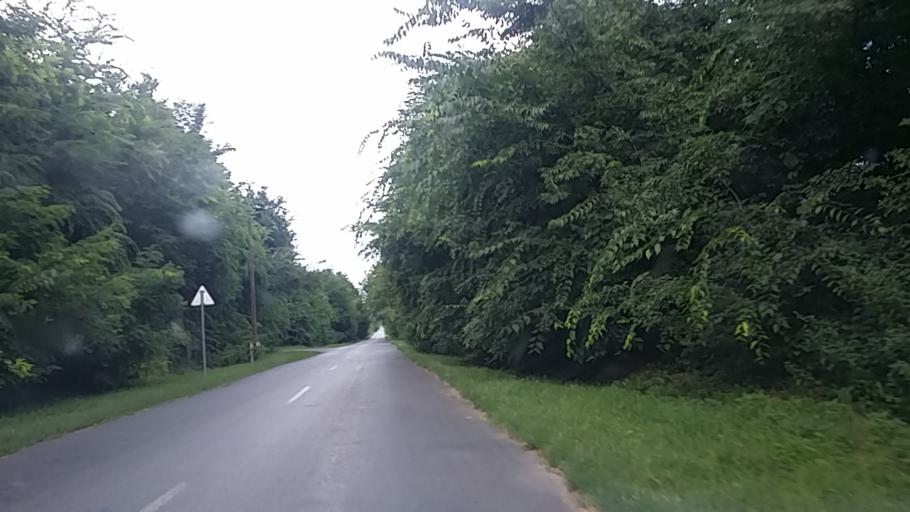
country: HU
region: Tolna
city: Szedres
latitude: 46.5251
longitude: 18.6392
